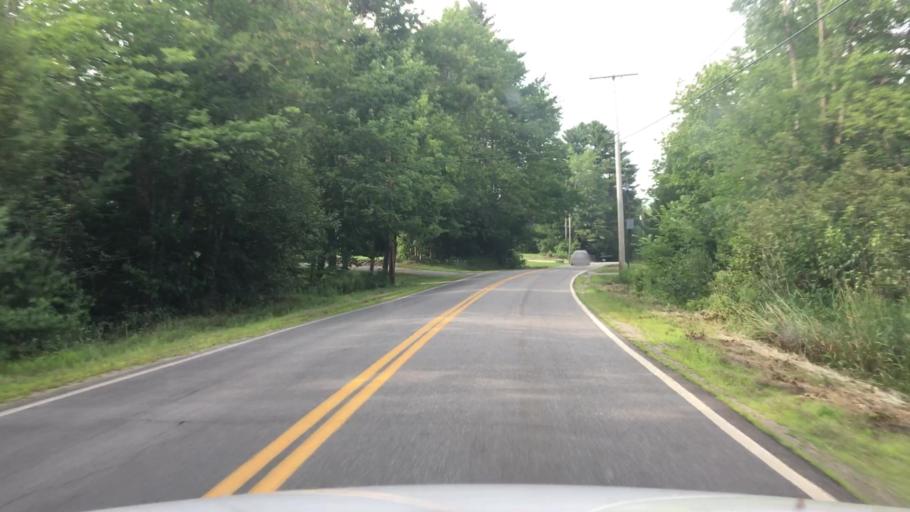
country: US
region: Maine
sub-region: Lincoln County
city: Waldoboro
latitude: 44.1737
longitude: -69.3789
